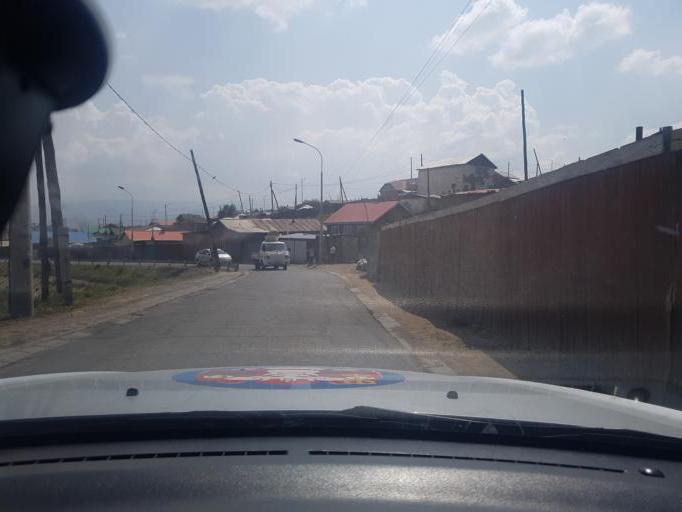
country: MN
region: Ulaanbaatar
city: Ulaanbaatar
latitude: 47.9387
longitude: 106.8981
